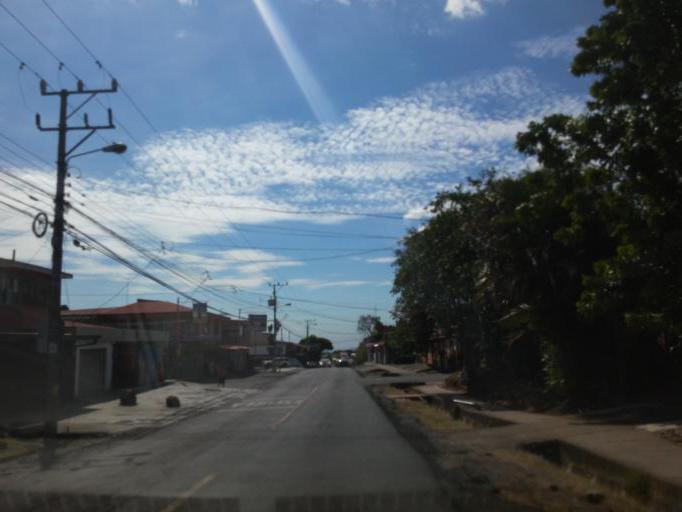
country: CR
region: Heredia
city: Santo Domingo
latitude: 10.0360
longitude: -84.1606
